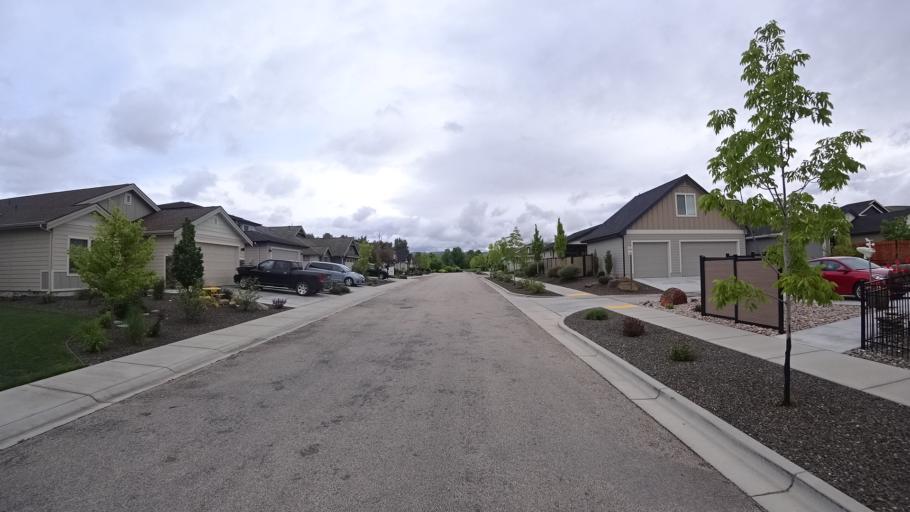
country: US
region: Idaho
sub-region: Ada County
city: Eagle
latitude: 43.7705
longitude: -116.2644
